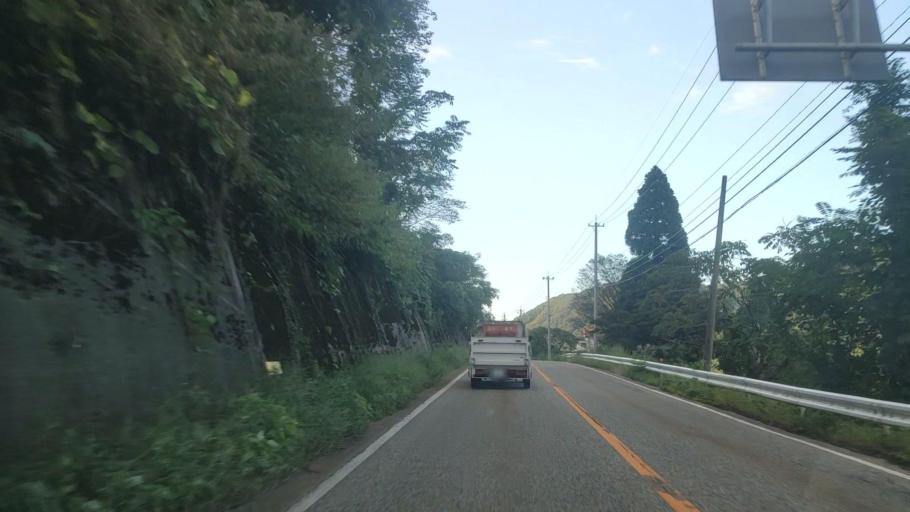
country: JP
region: Toyama
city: Nanto-shi
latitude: 36.5668
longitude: 136.9929
